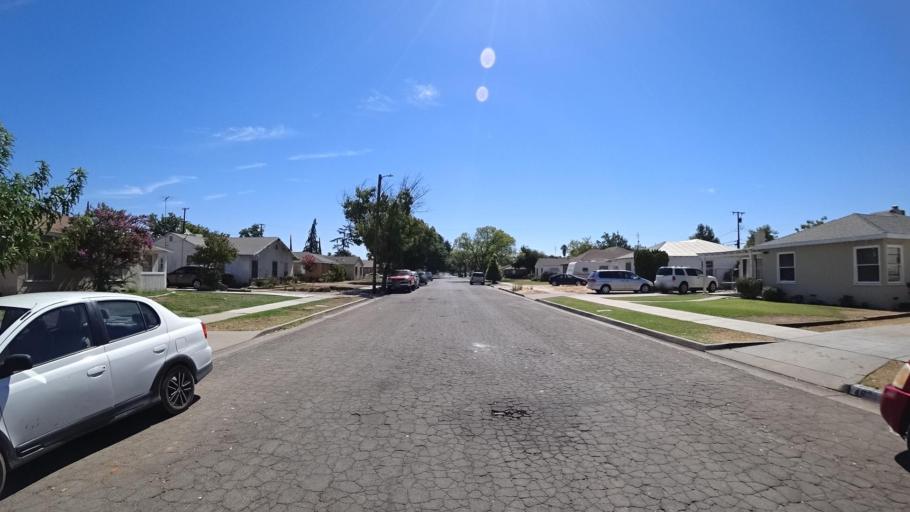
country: US
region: California
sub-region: Fresno County
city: Sunnyside
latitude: 36.7459
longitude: -119.7351
